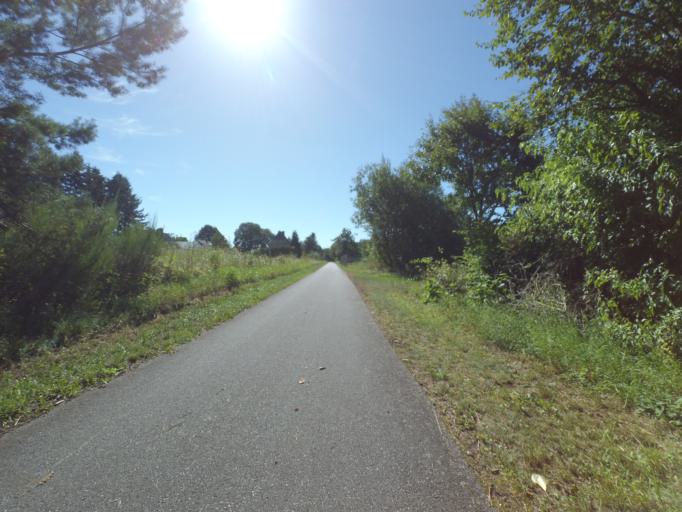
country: DE
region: Rheinland-Pfalz
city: Hasborn
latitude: 50.0561
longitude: 6.9119
